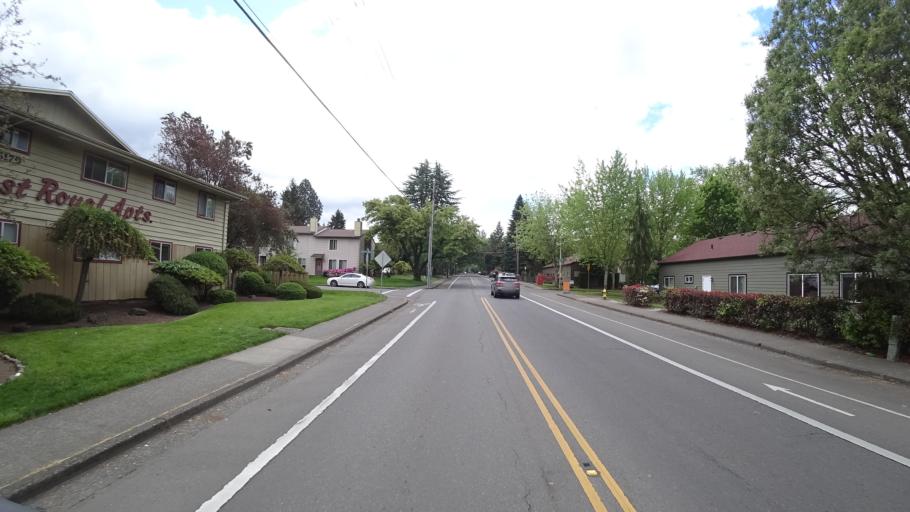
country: US
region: Oregon
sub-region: Washington County
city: Beaverton
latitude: 45.4754
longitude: -122.8003
